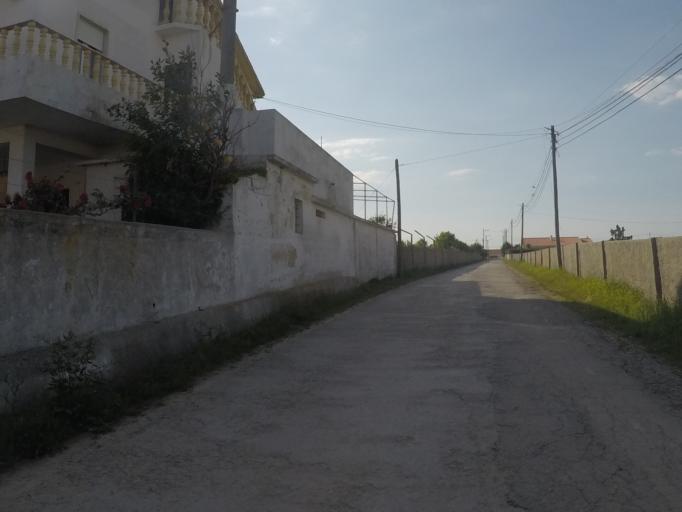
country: PT
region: Setubal
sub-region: Sesimbra
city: Sesimbra
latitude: 38.4299
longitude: -9.1871
